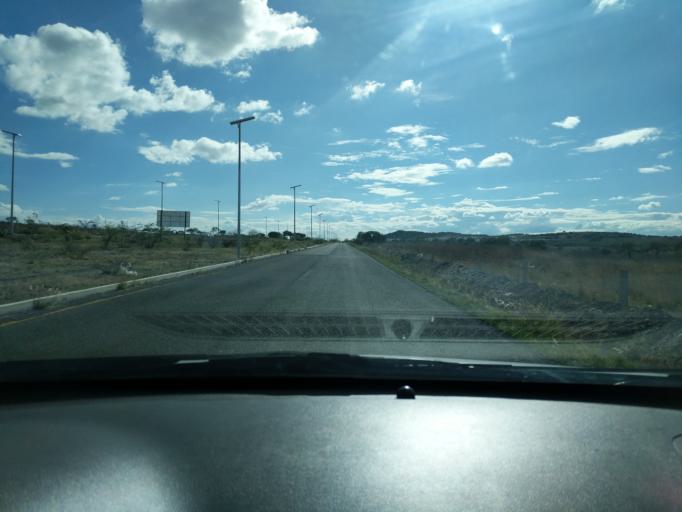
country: MX
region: Queretaro
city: La Canada
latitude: 20.5969
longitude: -100.2969
